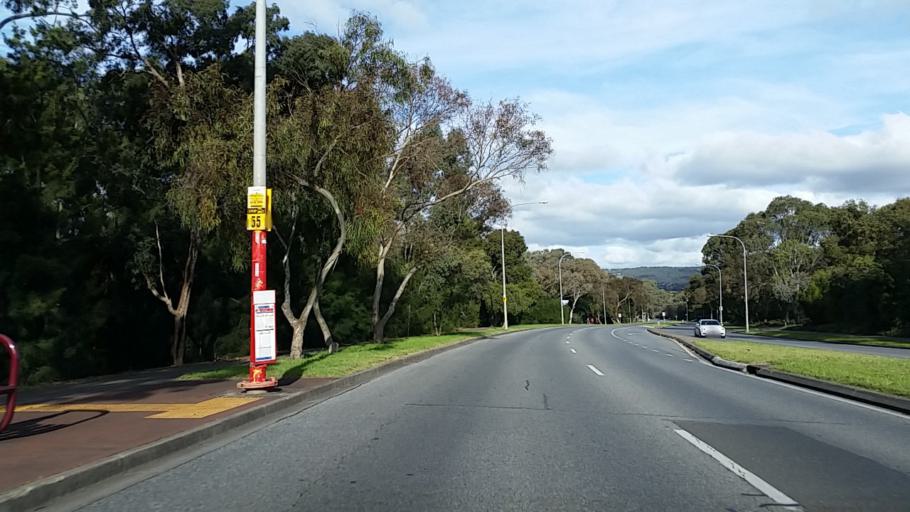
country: AU
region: South Australia
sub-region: Tea Tree Gully
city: Modbury
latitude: -34.8042
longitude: 138.6889
